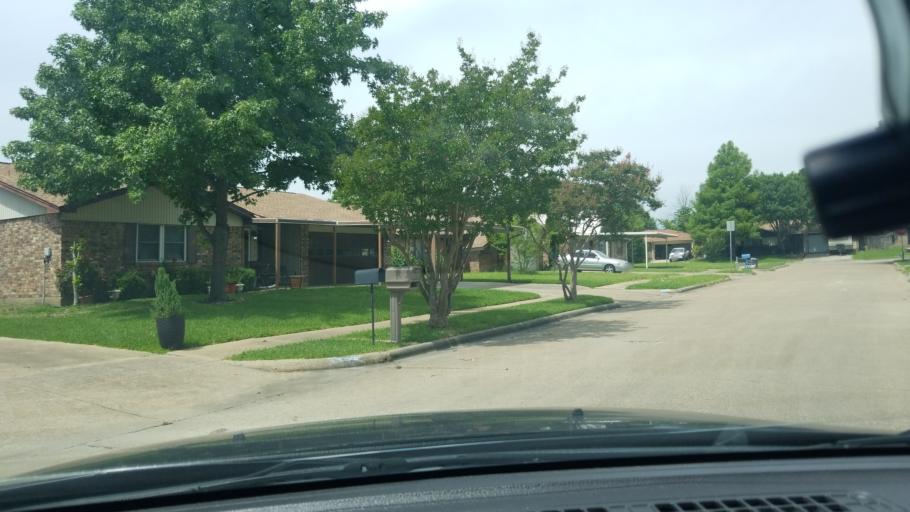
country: US
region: Texas
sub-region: Dallas County
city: Mesquite
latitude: 32.7574
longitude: -96.5783
